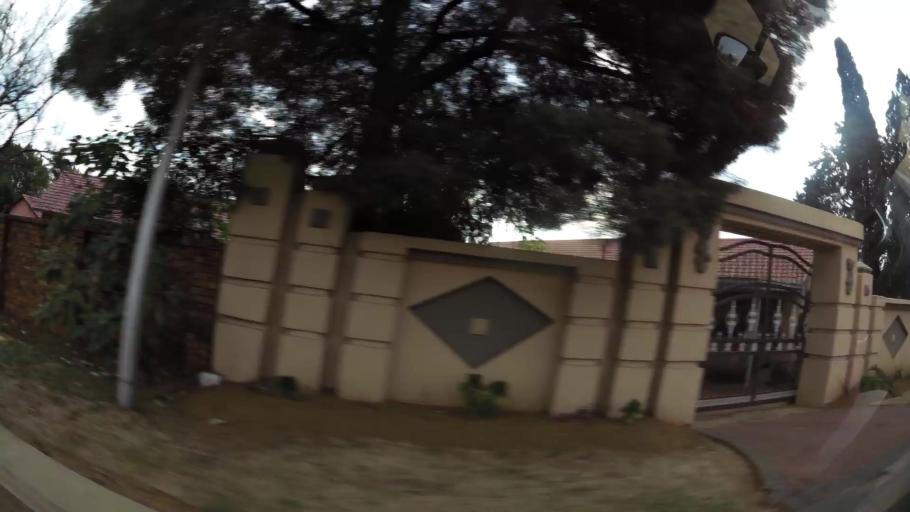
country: ZA
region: Gauteng
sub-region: Ekurhuleni Metropolitan Municipality
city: Benoni
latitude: -26.1304
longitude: 28.3605
